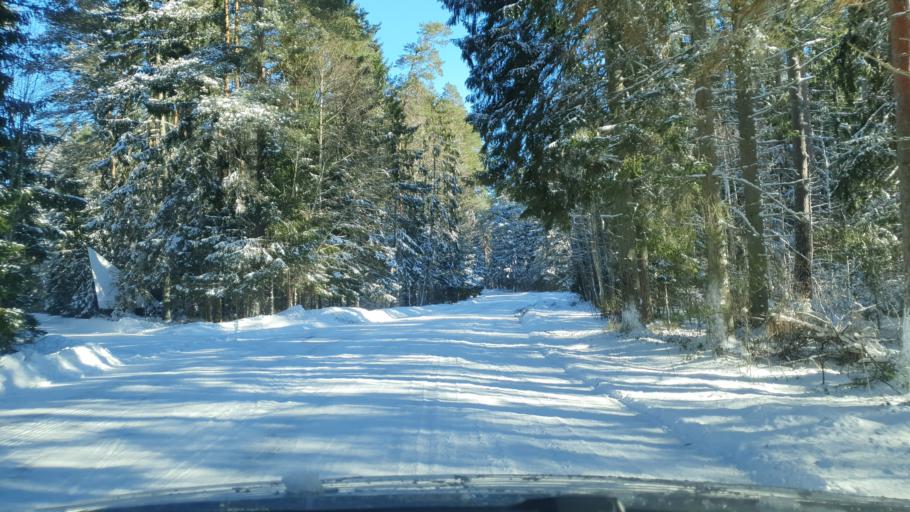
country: EE
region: Laeaene-Virumaa
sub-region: Haljala vald
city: Haljala
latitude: 59.6167
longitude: 26.0211
